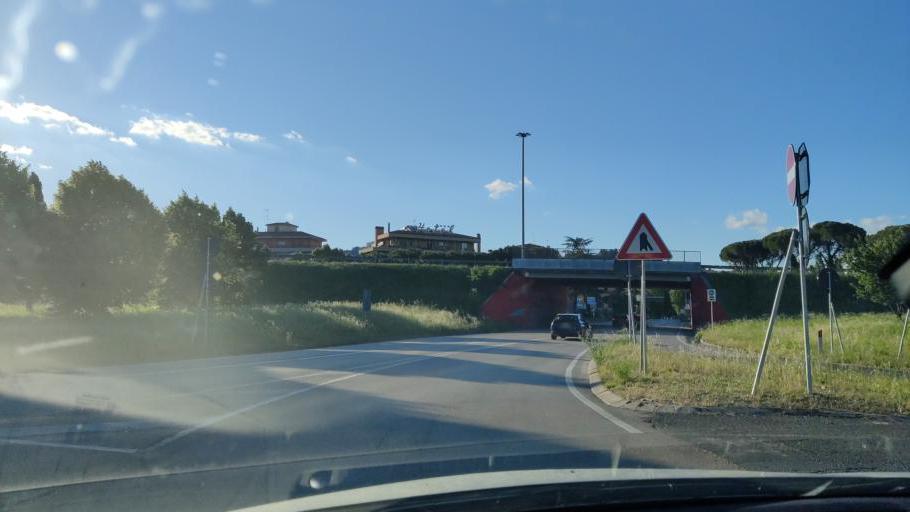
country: IT
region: Umbria
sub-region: Provincia di Perugia
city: Via Lippia
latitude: 43.0867
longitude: 12.4468
